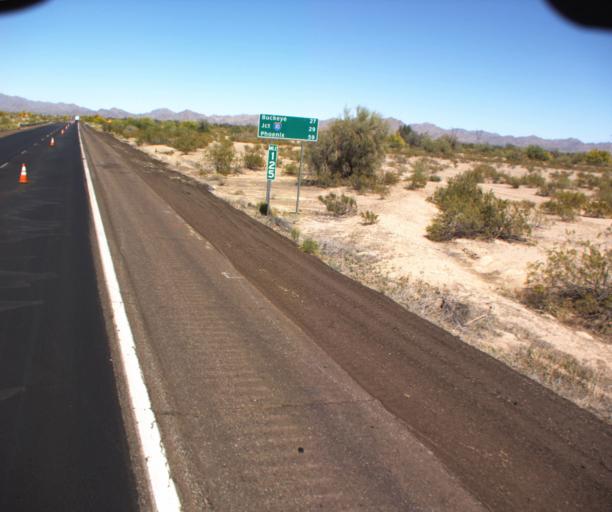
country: US
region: Arizona
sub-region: Maricopa County
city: Gila Bend
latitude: 33.0043
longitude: -112.6571
